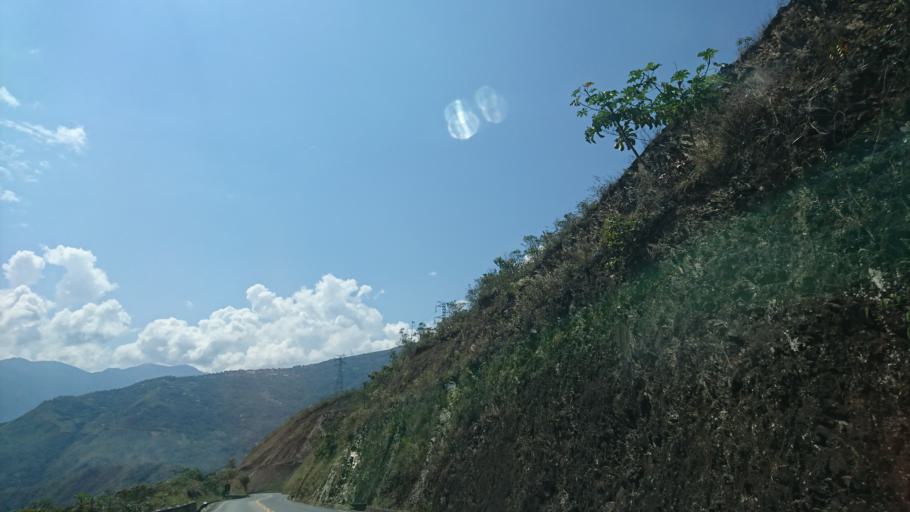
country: BO
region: La Paz
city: Coroico
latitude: -16.2031
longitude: -67.7635
